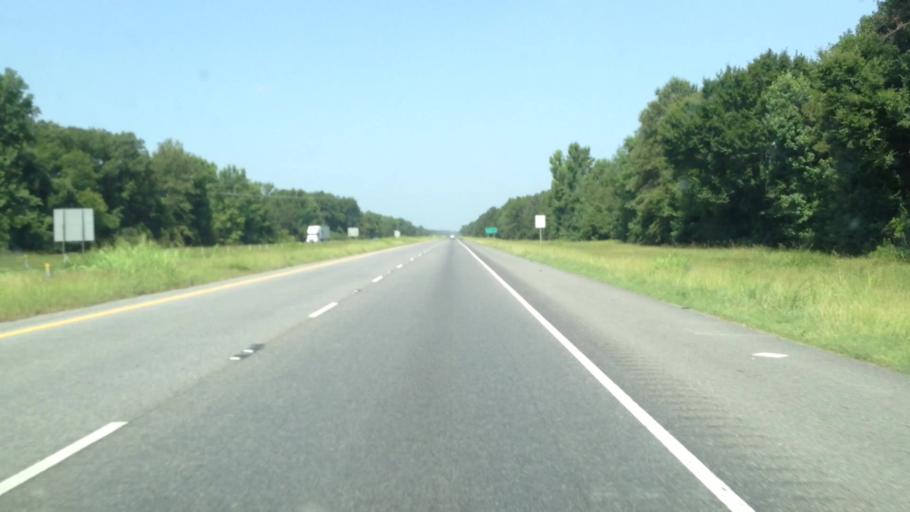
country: US
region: Louisiana
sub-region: Richland Parish
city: Delhi
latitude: 32.4450
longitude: -91.5064
